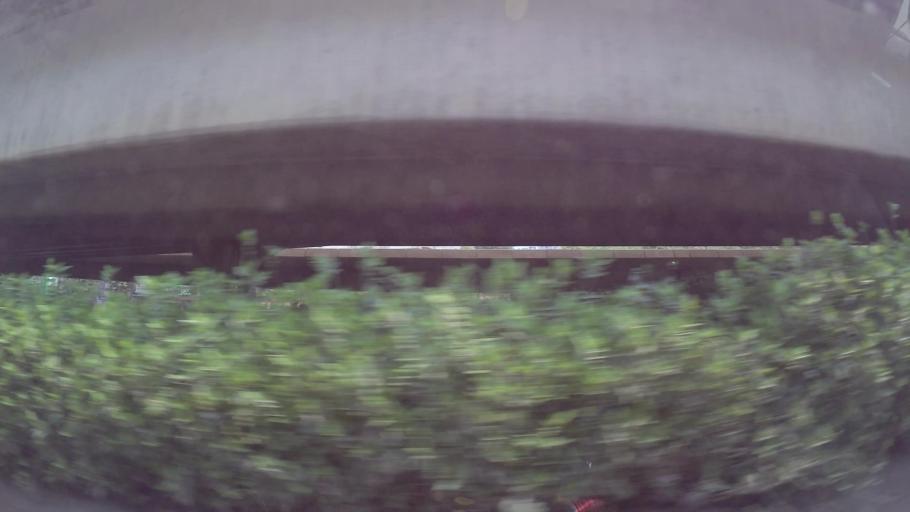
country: VN
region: Ha Noi
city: Thanh Xuan
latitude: 20.9943
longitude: 105.8008
